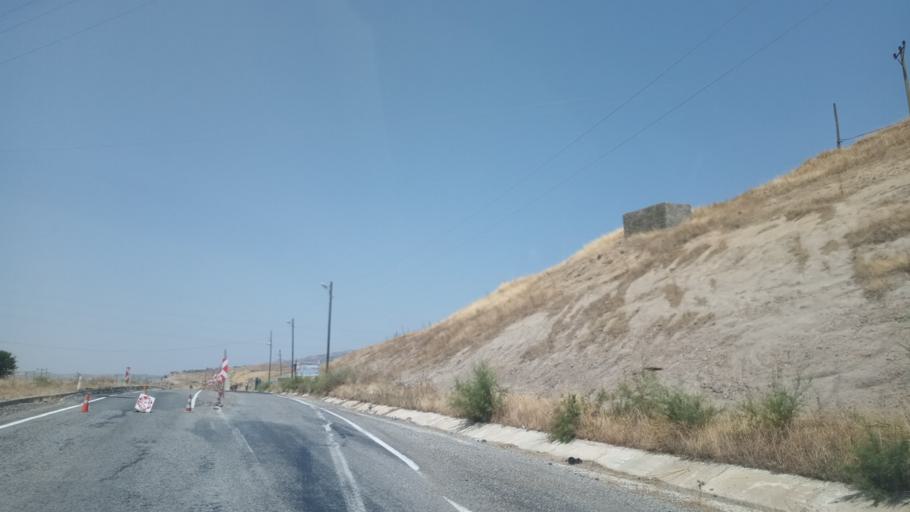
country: TR
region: Batman
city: Melefan
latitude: 38.1655
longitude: 41.5610
